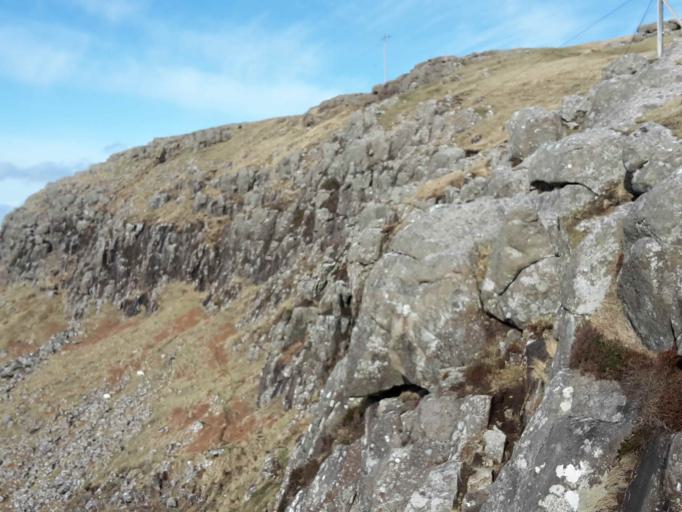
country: GB
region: Scotland
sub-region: Eilean Siar
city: Harris
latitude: 57.4292
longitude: -6.7793
